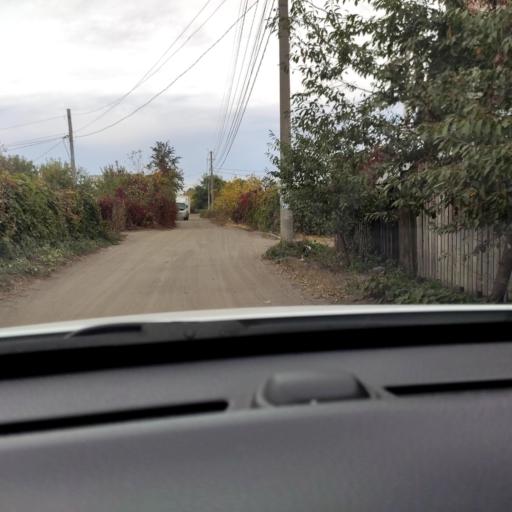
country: RU
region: Voronezj
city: Maslovka
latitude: 51.6042
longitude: 39.2781
